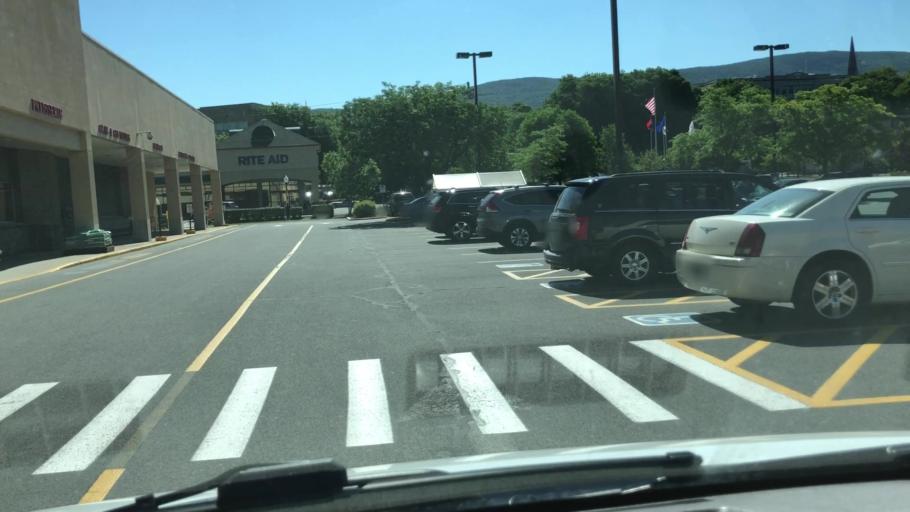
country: US
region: Massachusetts
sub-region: Berkshire County
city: North Adams
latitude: 42.7009
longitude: -73.1110
